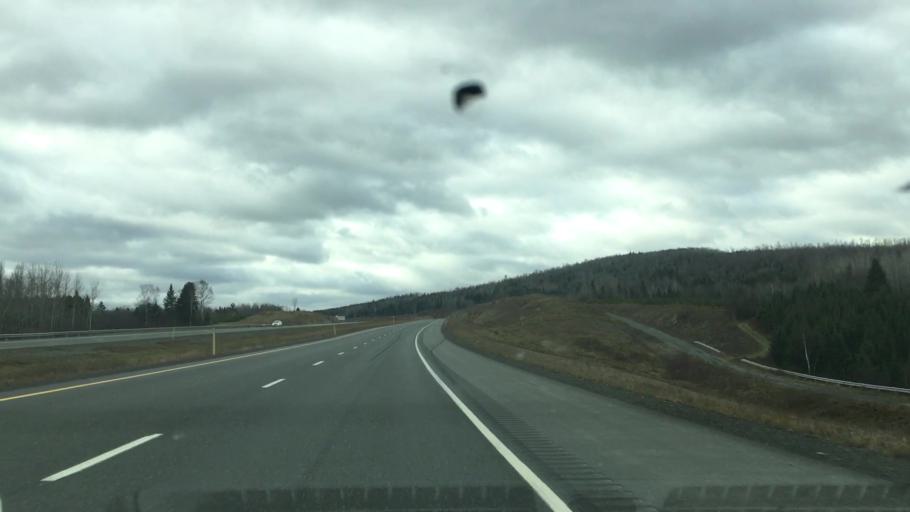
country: US
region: Maine
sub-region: Aroostook County
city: Fort Fairfield
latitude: 46.7325
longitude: -67.7219
